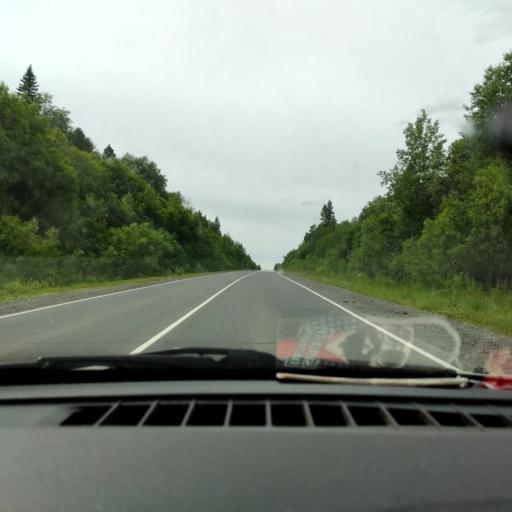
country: RU
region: Perm
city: Chusovoy
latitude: 58.3709
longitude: 58.0263
